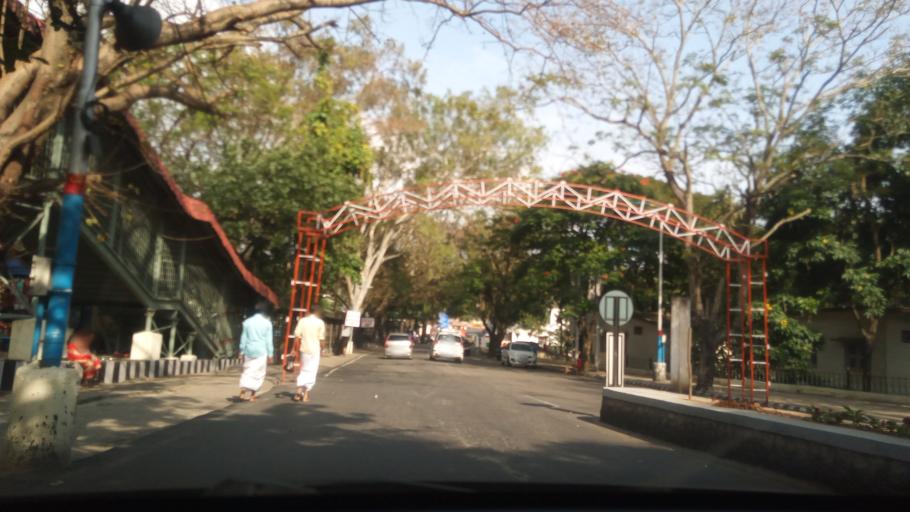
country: IN
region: Andhra Pradesh
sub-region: Chittoor
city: Tirumala
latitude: 13.6802
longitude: 79.3490
